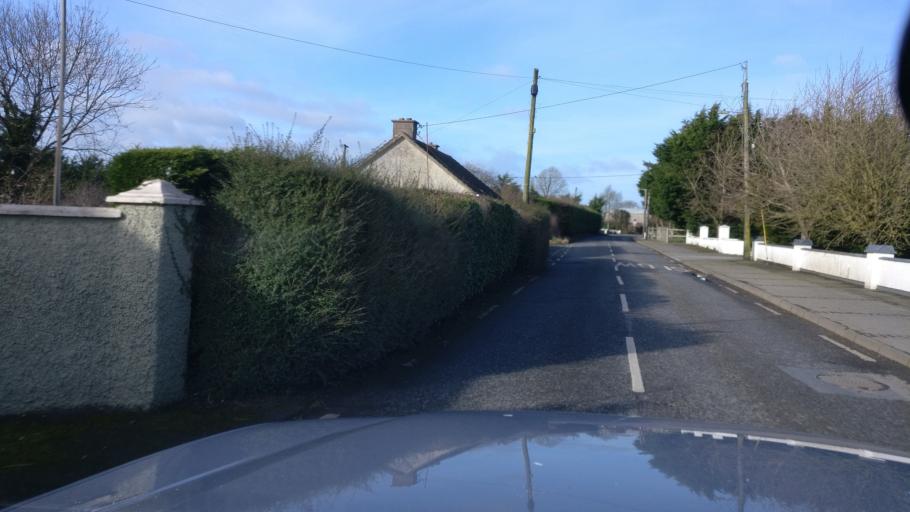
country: IE
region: Leinster
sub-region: Kilkenny
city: Castlecomer
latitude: 52.8614
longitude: -7.1636
